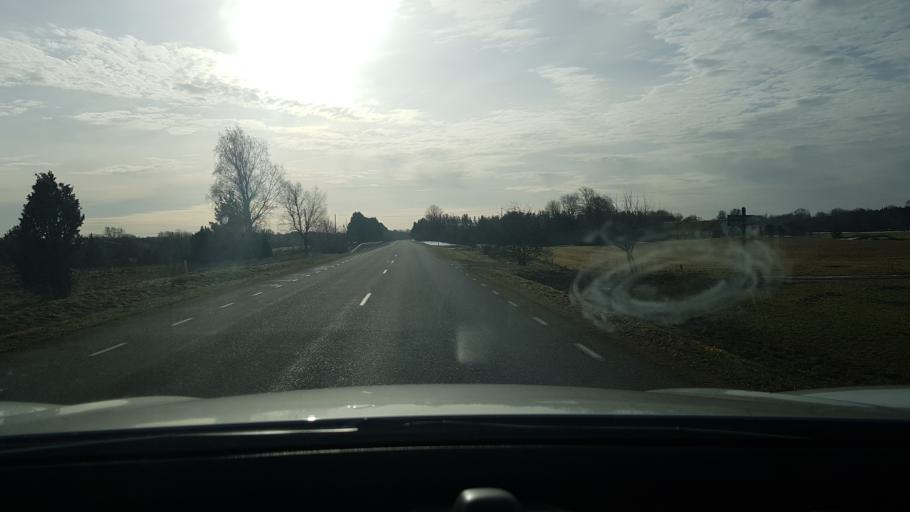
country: EE
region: Saare
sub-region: Kuressaare linn
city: Kuressaare
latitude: 58.5194
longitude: 22.7026
